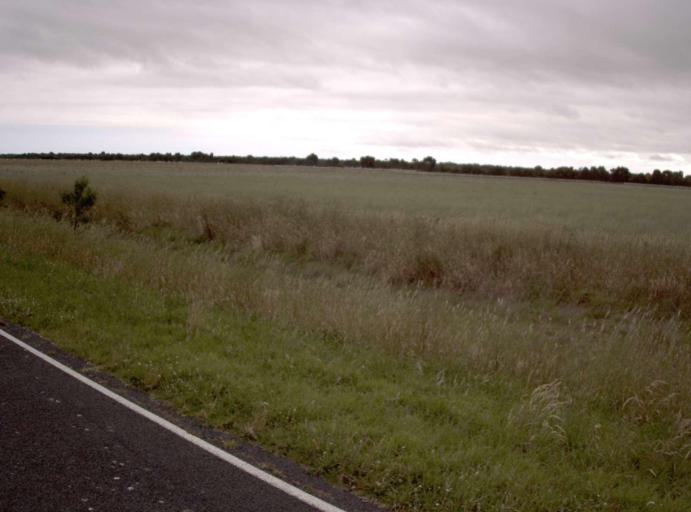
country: AU
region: Victoria
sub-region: Wellington
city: Sale
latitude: -38.5600
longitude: 146.8806
